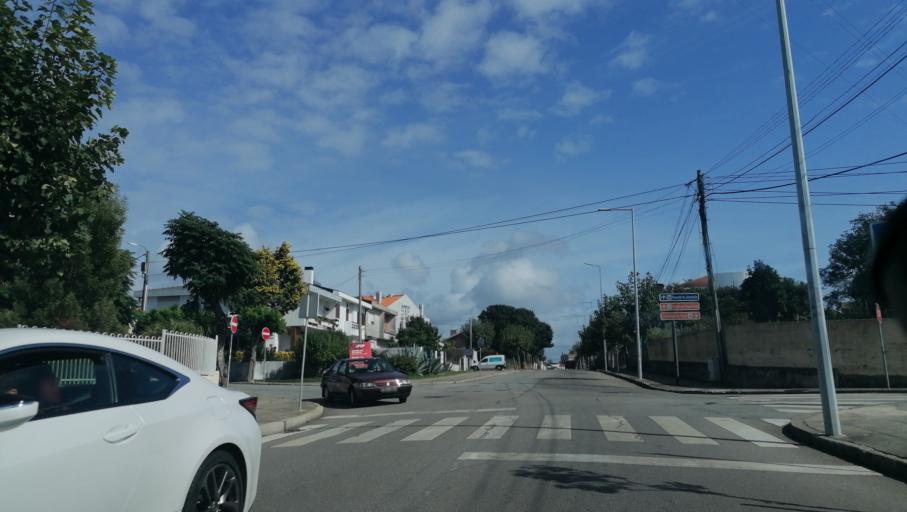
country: PT
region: Aveiro
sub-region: Espinho
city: Silvalde
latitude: 41.0040
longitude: -8.6270
